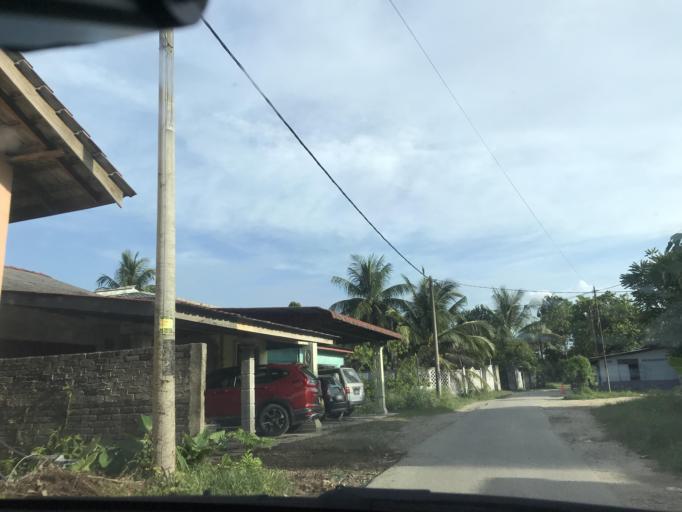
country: MY
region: Kelantan
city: Kota Bharu
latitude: 6.1330
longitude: 102.2228
